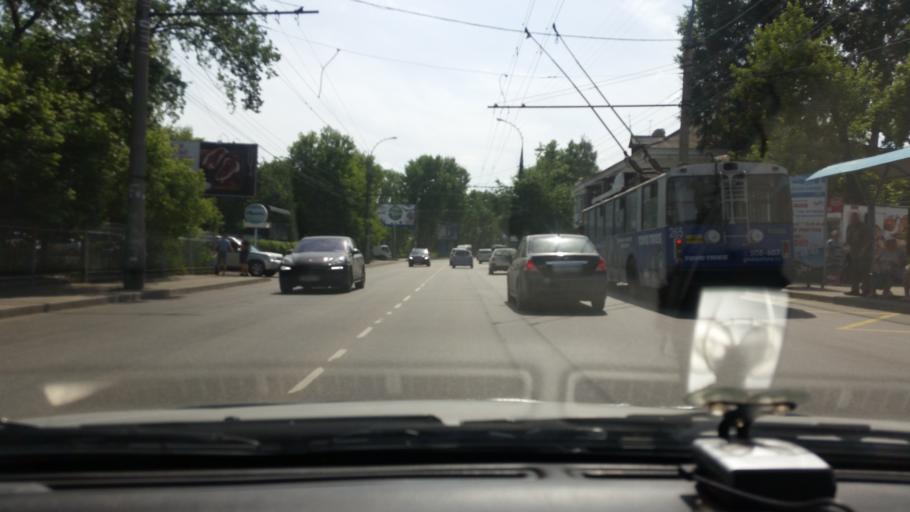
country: RU
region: Irkutsk
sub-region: Irkutskiy Rayon
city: Irkutsk
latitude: 52.2321
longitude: 104.3155
